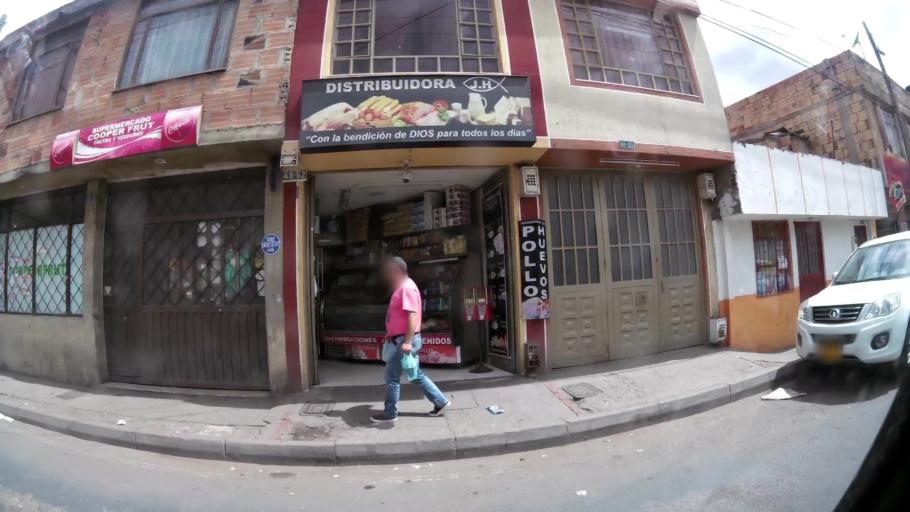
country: CO
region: Cundinamarca
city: Funza
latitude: 4.7159
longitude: -74.1385
